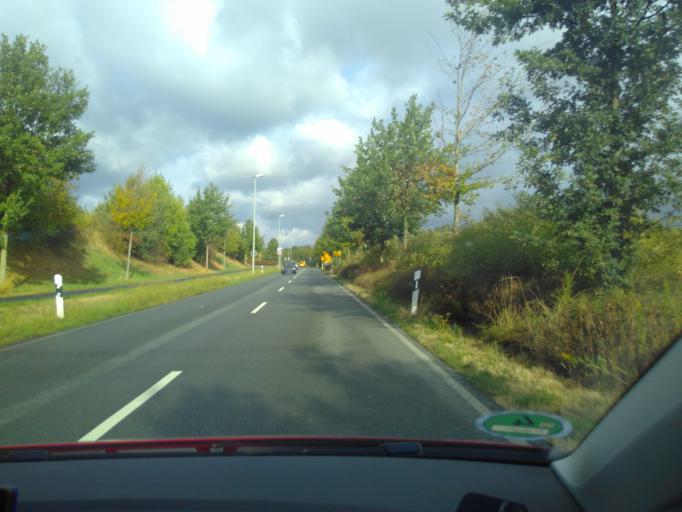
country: DE
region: North Rhine-Westphalia
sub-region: Regierungsbezirk Munster
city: Warendorf
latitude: 51.9612
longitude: 8.0070
